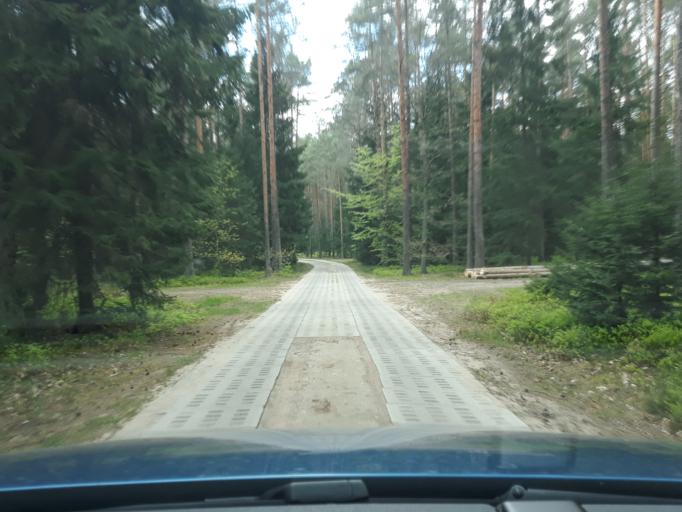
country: PL
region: Pomeranian Voivodeship
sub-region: Powiat czluchowski
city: Czluchow
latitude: 53.7430
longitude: 17.3441
